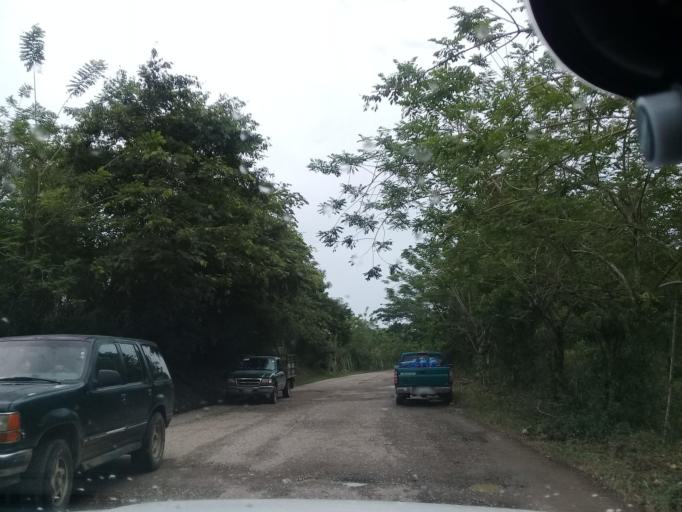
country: MX
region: Veracruz
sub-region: Chalma
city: San Pedro Coyutla
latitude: 21.2124
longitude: -98.3819
